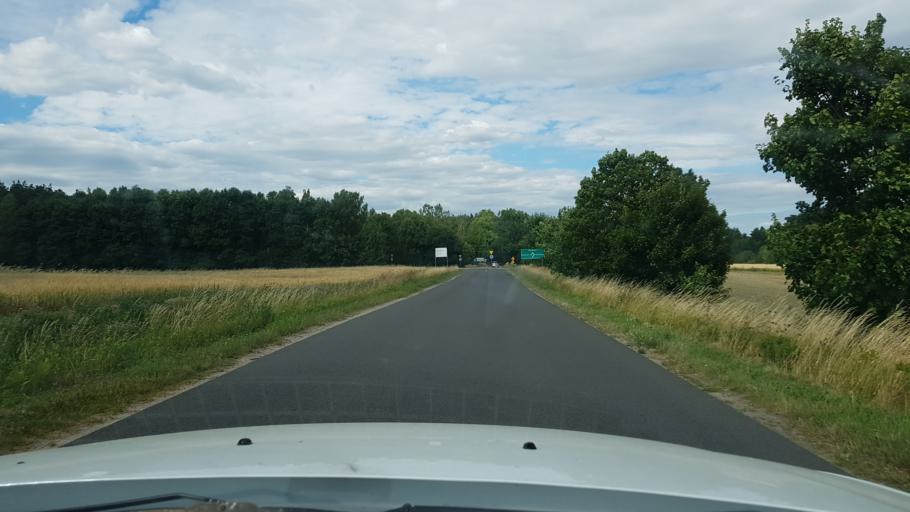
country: PL
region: West Pomeranian Voivodeship
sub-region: Powiat drawski
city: Wierzchowo
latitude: 53.4477
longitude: 16.0780
